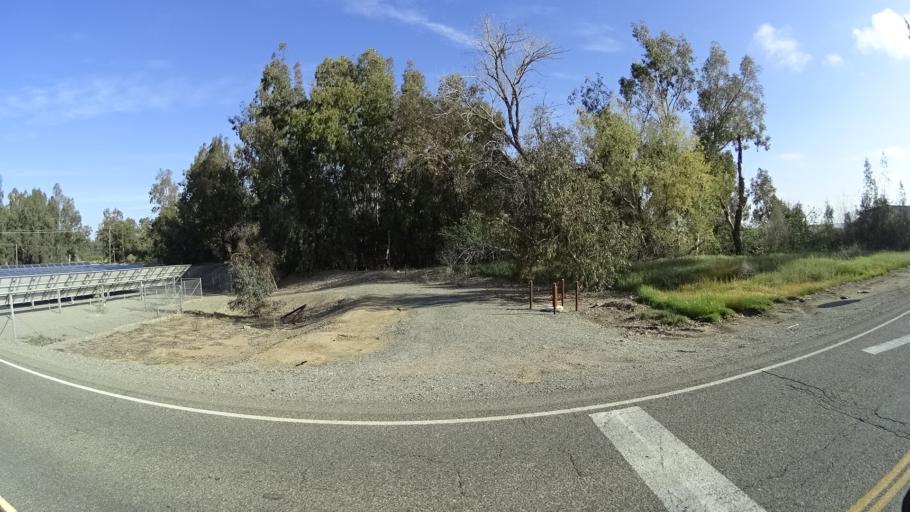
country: US
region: California
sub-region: Glenn County
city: Willows
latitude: 39.5837
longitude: -122.1922
